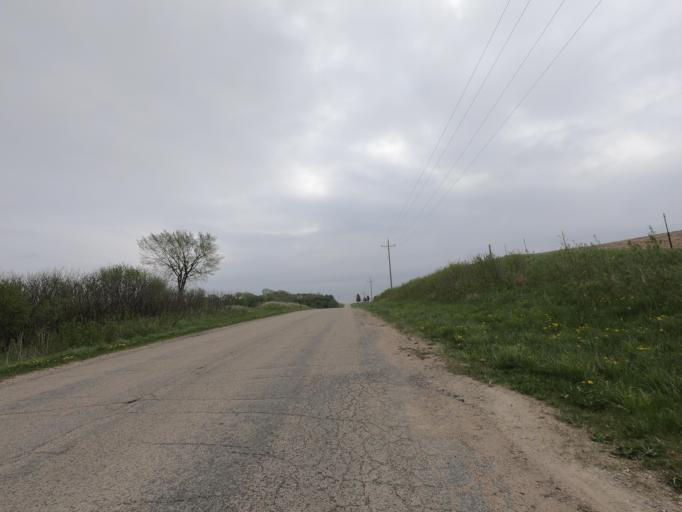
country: US
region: Wisconsin
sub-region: Jefferson County
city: Jefferson
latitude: 43.0319
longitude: -88.7882
